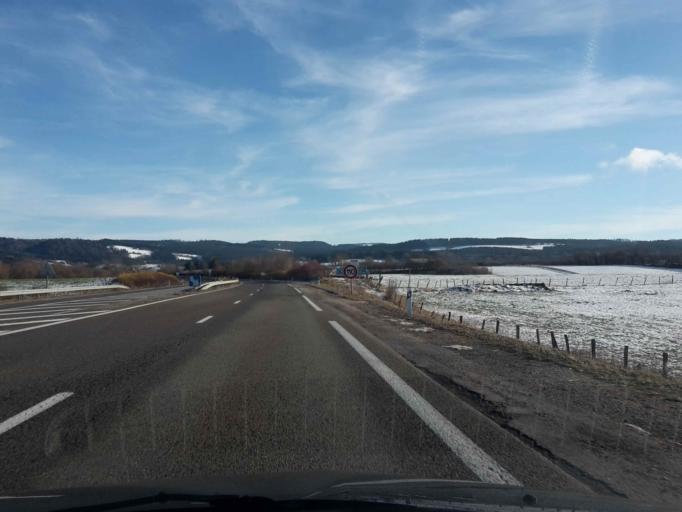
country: FR
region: Franche-Comte
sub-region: Departement du Doubs
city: Valdahon
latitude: 47.1046
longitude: 6.3235
